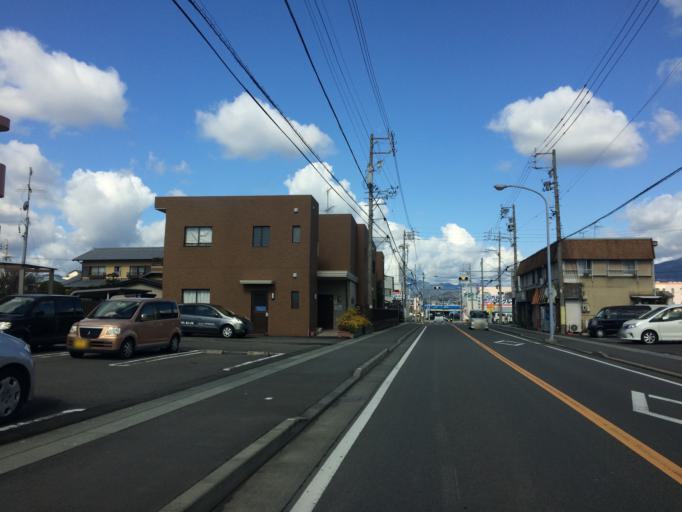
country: JP
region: Shizuoka
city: Shizuoka-shi
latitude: 34.9856
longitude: 138.4258
